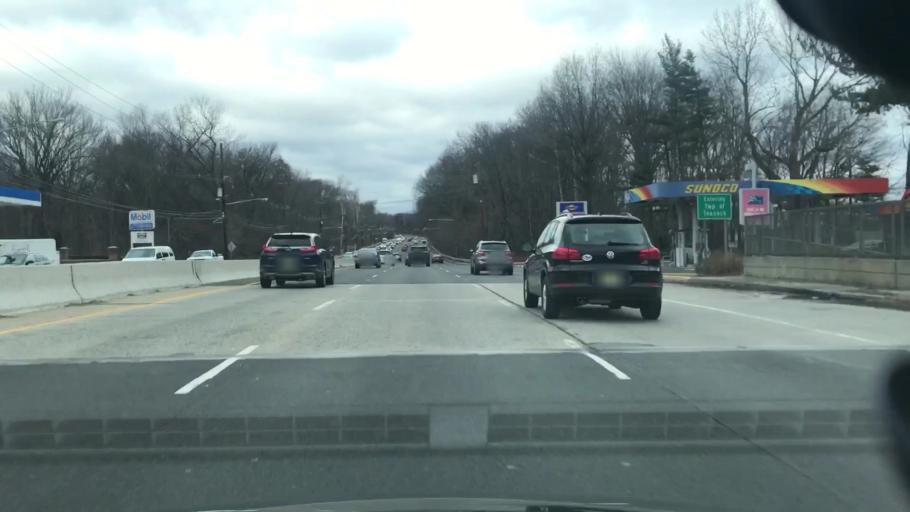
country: US
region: New Jersey
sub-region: Bergen County
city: Englewood
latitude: 40.8836
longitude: -73.9886
